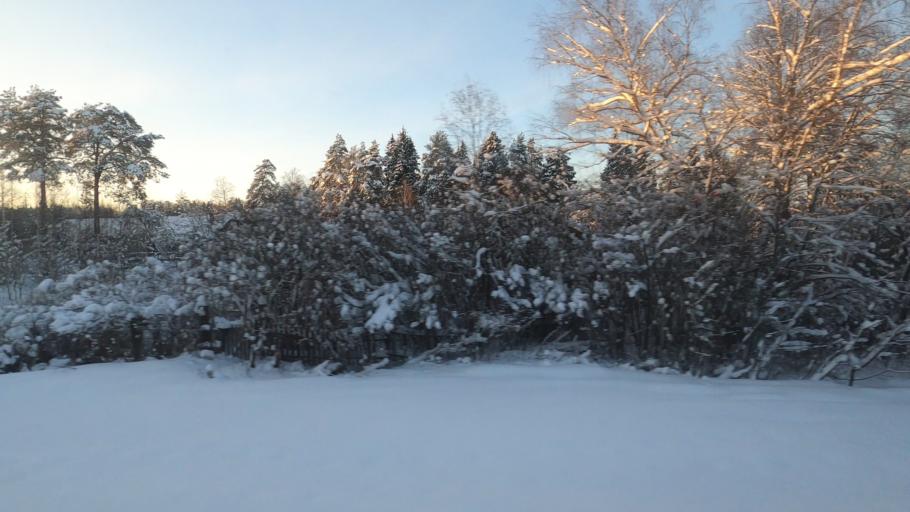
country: RU
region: Moskovskaya
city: Novo-Nikol'skoye
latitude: 56.5487
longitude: 37.5610
